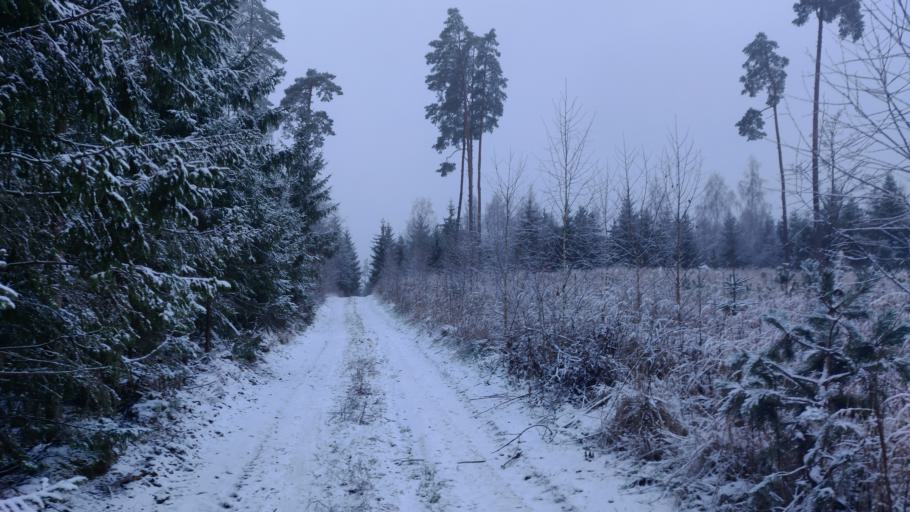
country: LT
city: Trakai
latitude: 54.5966
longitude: 24.9651
